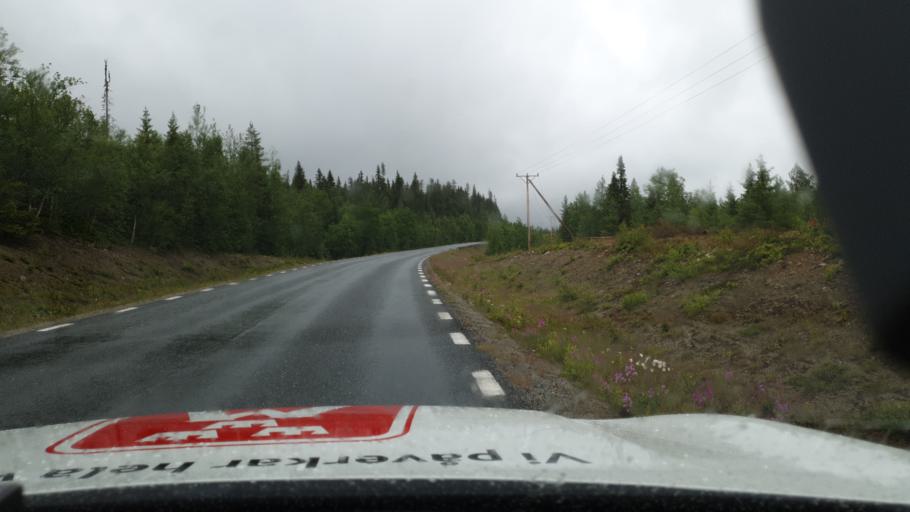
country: SE
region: Vaesterbotten
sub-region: Lycksele Kommun
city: Soderfors
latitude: 64.3818
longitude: 17.9893
